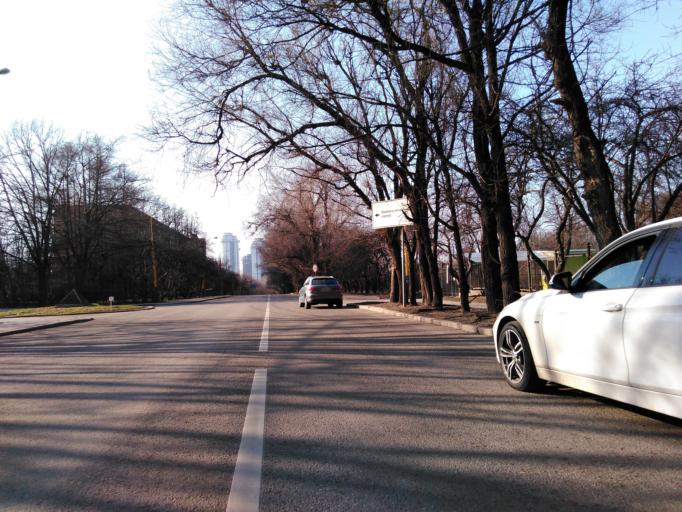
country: RU
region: Moscow
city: Vorob'yovo
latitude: 55.7051
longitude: 37.5241
